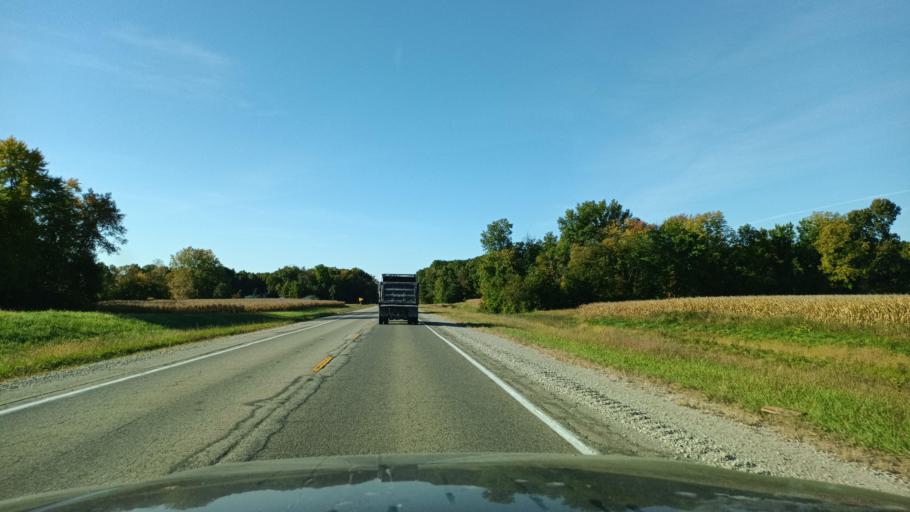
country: US
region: Illinois
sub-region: Clark County
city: Marshall
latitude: 39.4430
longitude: -87.6834
